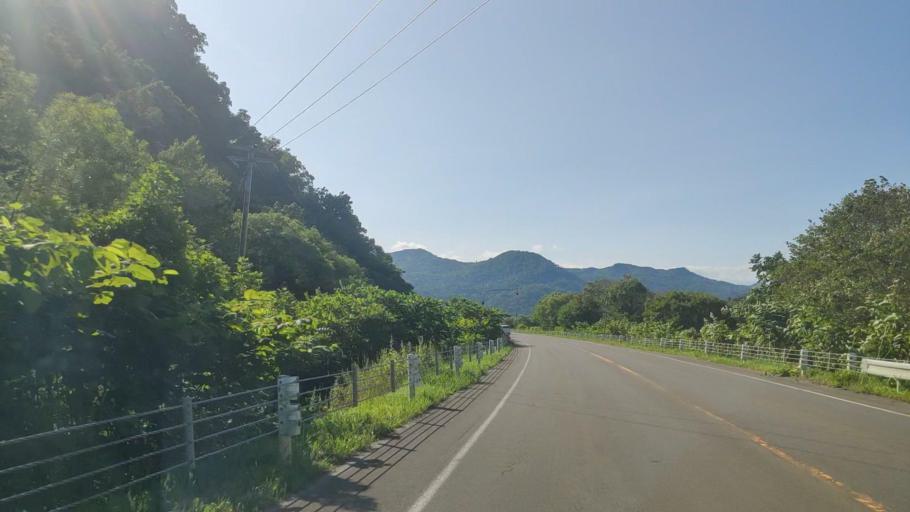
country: JP
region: Hokkaido
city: Nayoro
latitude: 44.7302
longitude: 142.2103
